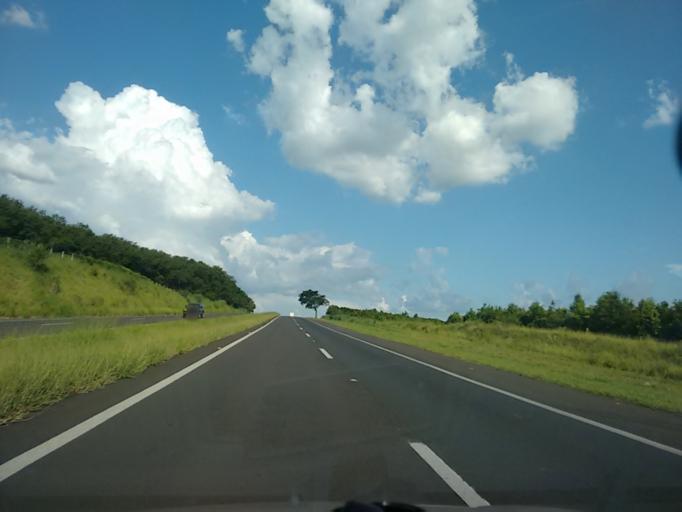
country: BR
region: Sao Paulo
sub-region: Duartina
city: Duartina
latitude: -22.3277
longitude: -49.4700
